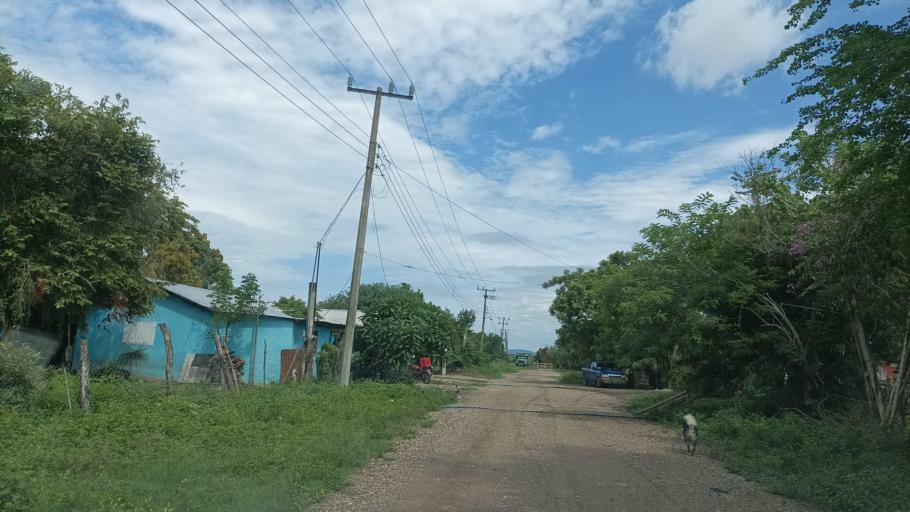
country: MX
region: Veracruz
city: Panuco
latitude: 21.9503
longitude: -98.1376
